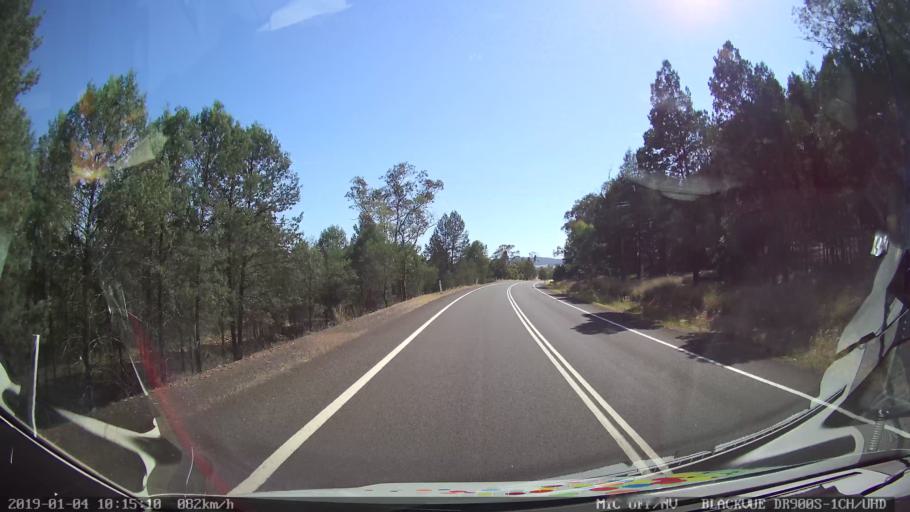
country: AU
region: New South Wales
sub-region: Cabonne
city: Canowindra
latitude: -33.3888
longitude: 148.4179
